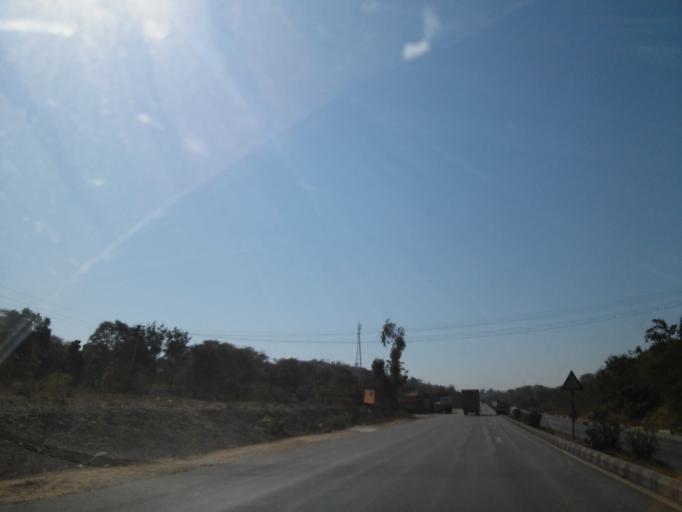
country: IN
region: Rajasthan
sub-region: Dungarpur
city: Dungarpur
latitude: 24.1802
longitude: 73.6868
